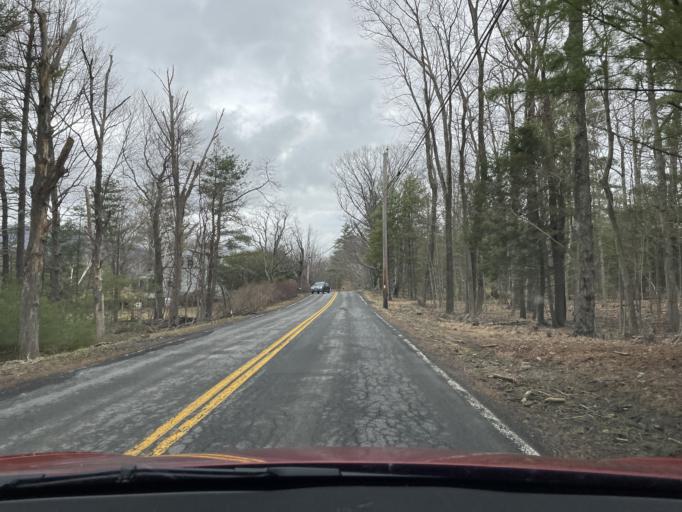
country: US
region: New York
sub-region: Ulster County
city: Manorville
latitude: 42.0896
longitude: -74.0591
